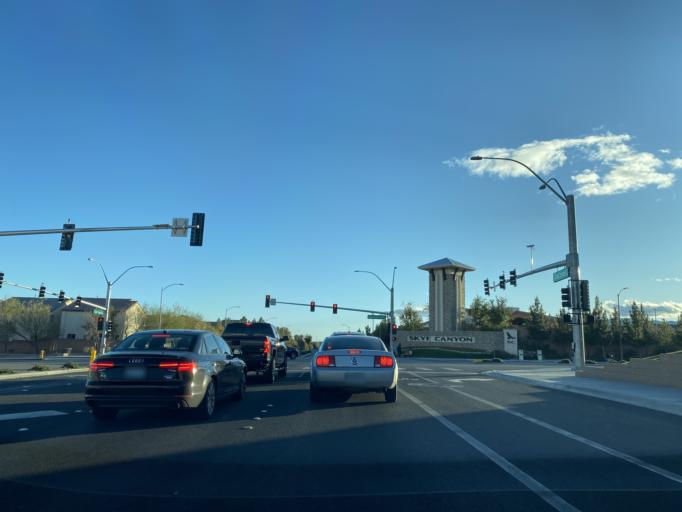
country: US
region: Nevada
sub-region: Clark County
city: Summerlin South
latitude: 36.3145
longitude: -115.3061
